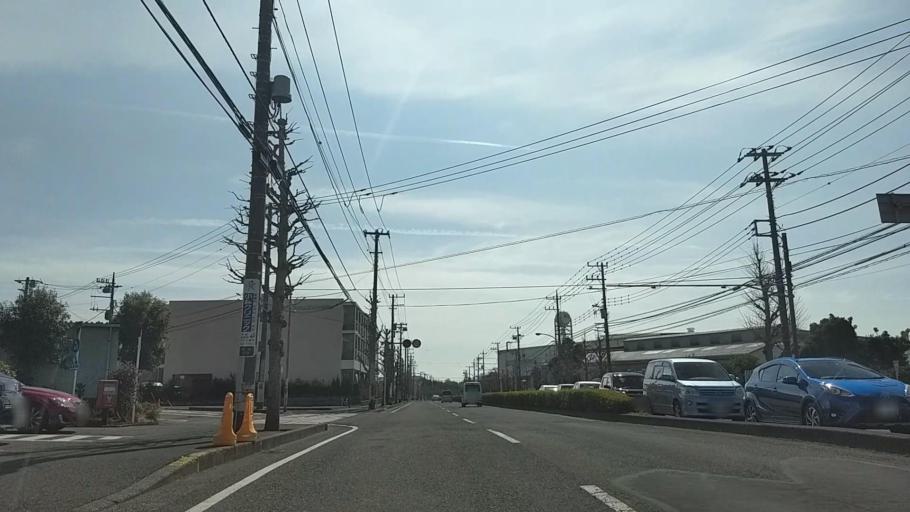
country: JP
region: Kanagawa
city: Fujisawa
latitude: 35.3892
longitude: 139.4575
